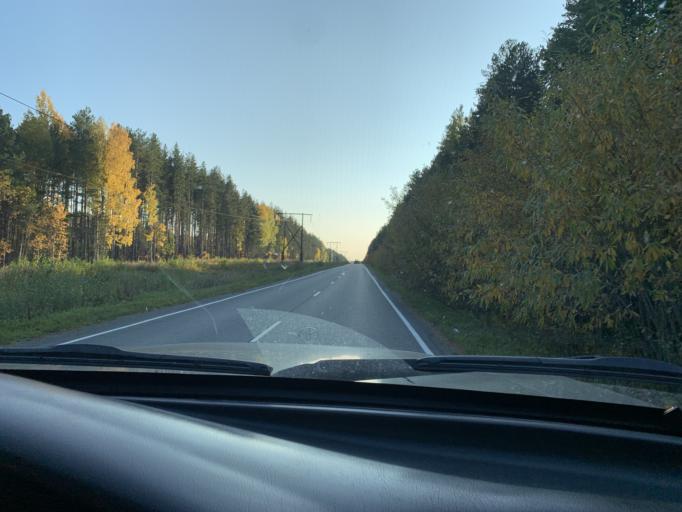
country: RU
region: Sverdlovsk
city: Verkhneye Dubrovo
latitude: 56.8694
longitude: 61.0986
